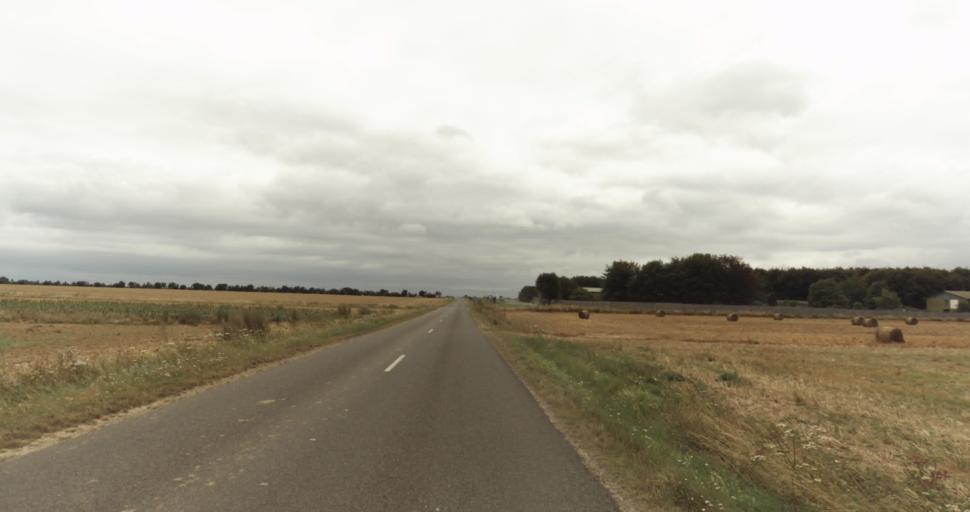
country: FR
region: Haute-Normandie
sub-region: Departement de l'Eure
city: Gravigny
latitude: 49.0475
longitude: 1.2297
